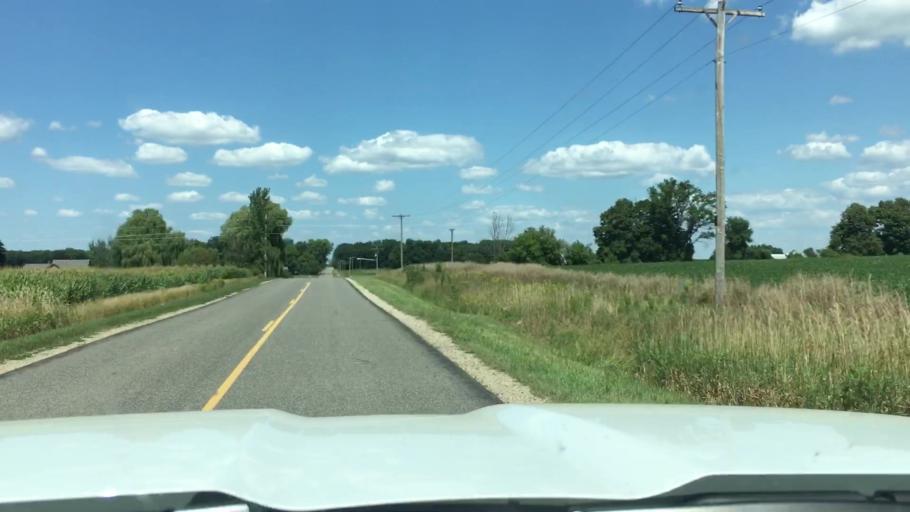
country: US
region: Michigan
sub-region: Muskegon County
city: Ravenna
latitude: 43.2484
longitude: -85.9179
